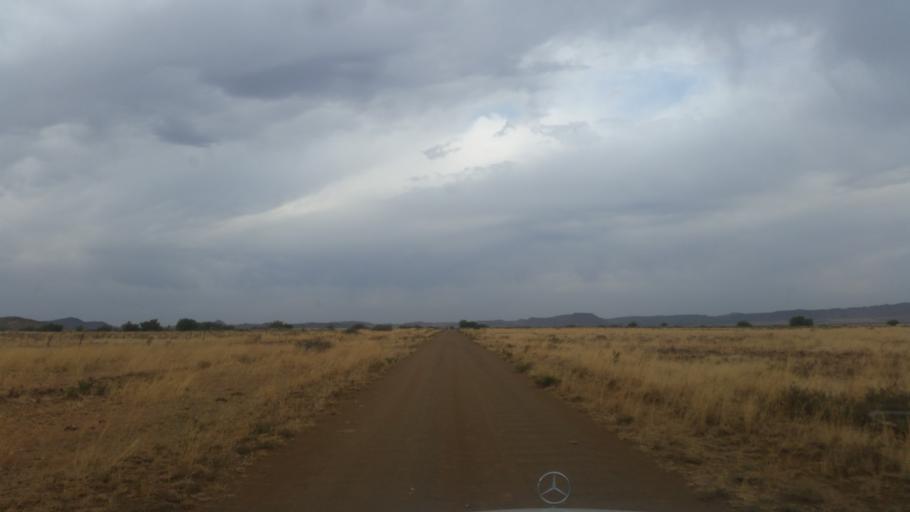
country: ZA
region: Orange Free State
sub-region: Xhariep District Municipality
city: Trompsburg
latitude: -30.5069
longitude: 25.9325
